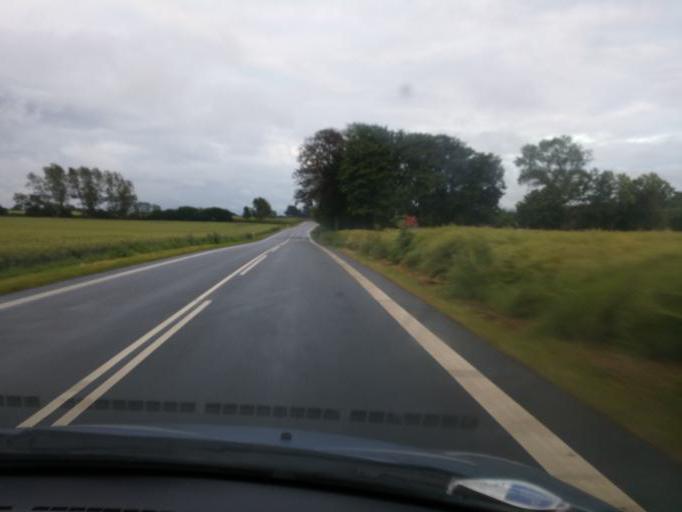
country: DK
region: South Denmark
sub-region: Kerteminde Kommune
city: Kerteminde
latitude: 55.4807
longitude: 10.6617
